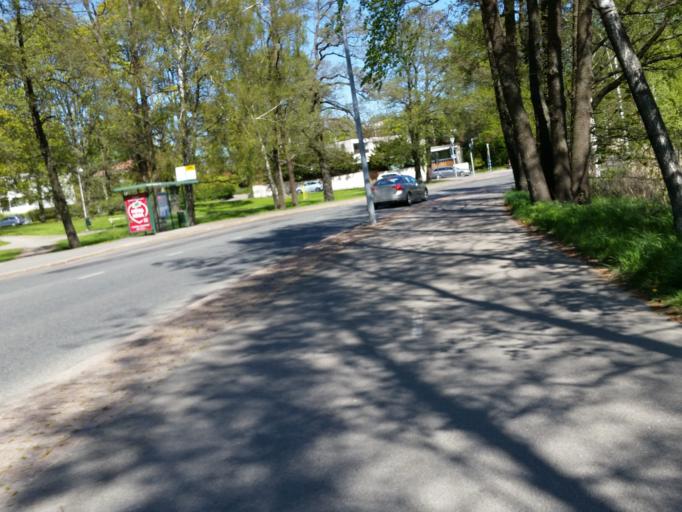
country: FI
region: Uusimaa
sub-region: Helsinki
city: Teekkarikylae
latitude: 60.1920
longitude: 24.8780
